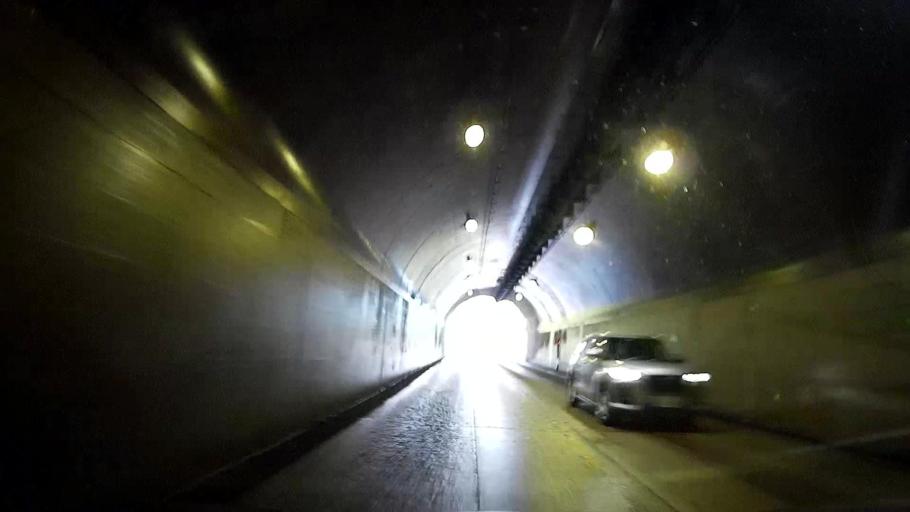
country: JP
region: Niigata
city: Shiozawa
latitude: 36.9106
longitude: 138.7938
